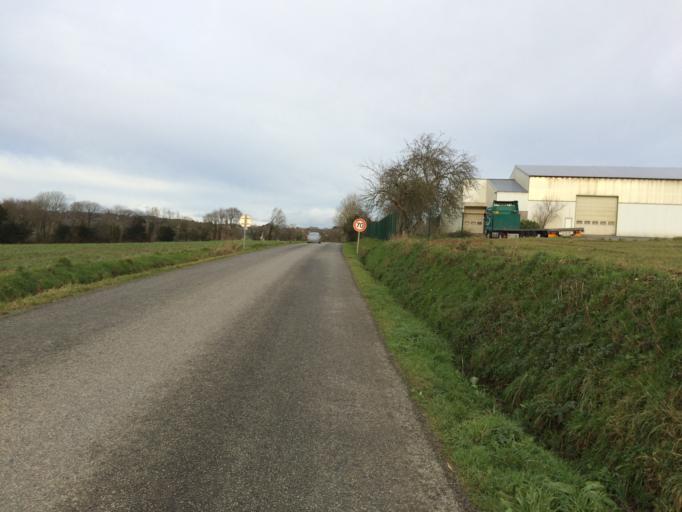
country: FR
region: Brittany
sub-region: Departement du Finistere
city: Saint-Urbain
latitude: 48.3890
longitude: -4.2345
